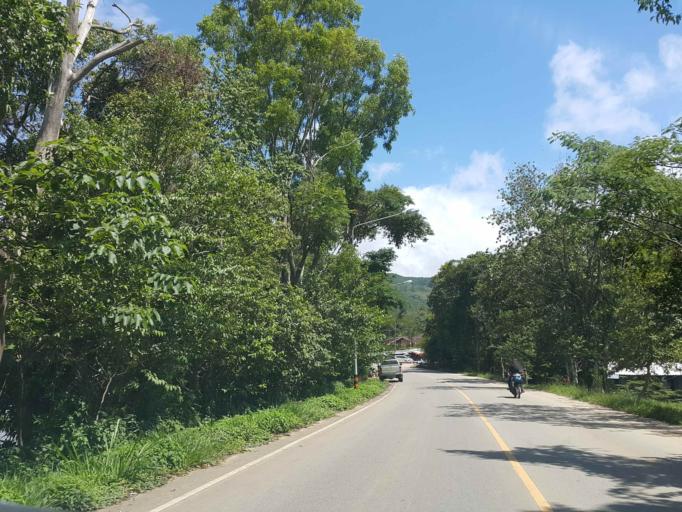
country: TH
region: Chiang Mai
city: Mae Chaem
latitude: 18.5327
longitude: 98.5218
